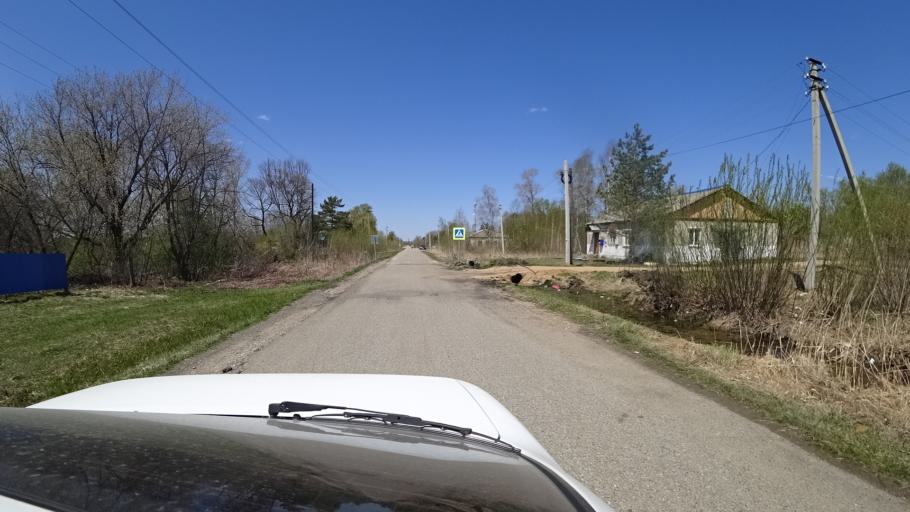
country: RU
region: Primorskiy
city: Lazo
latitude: 45.7947
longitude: 133.7659
